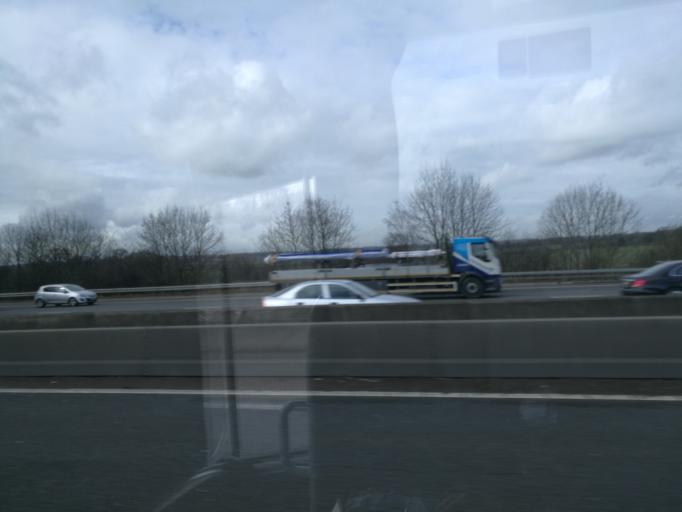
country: GB
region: England
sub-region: Hertfordshire
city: Flamstead
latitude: 51.8346
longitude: -0.4193
